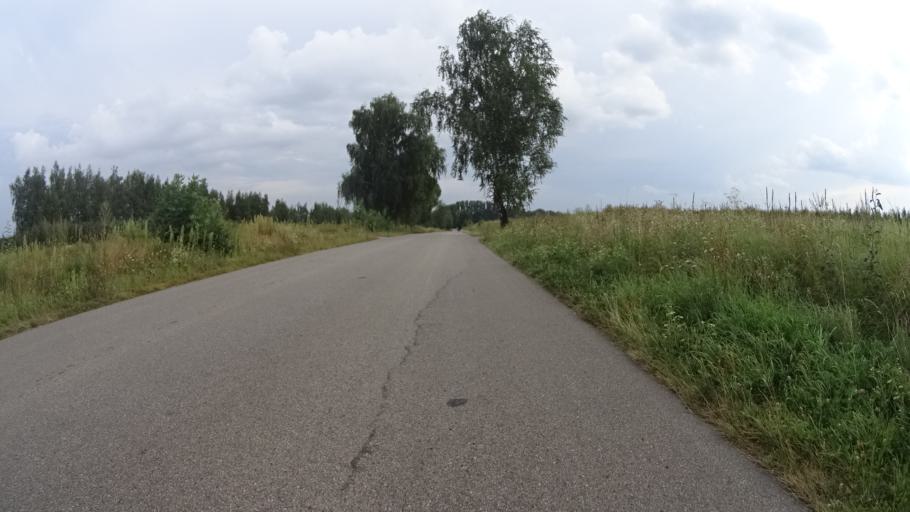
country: PL
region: Masovian Voivodeship
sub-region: Powiat grojecki
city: Goszczyn
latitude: 51.6940
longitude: 20.8568
